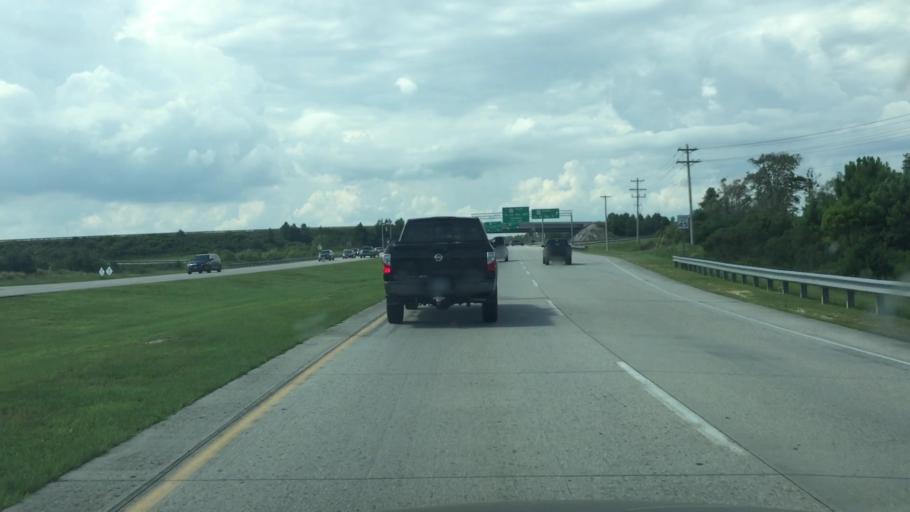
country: US
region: South Carolina
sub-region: Horry County
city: North Myrtle Beach
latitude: 33.8407
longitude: -78.6996
